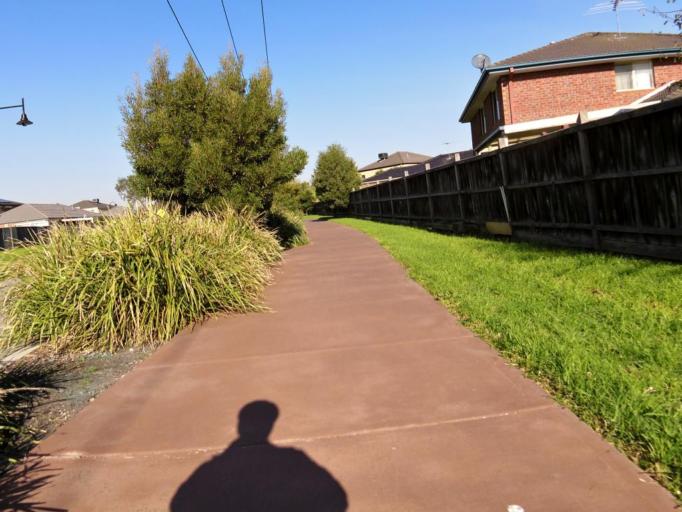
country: AU
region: Victoria
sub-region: Kingston
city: Aspendale Gardens
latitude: -38.0180
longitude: 145.1222
